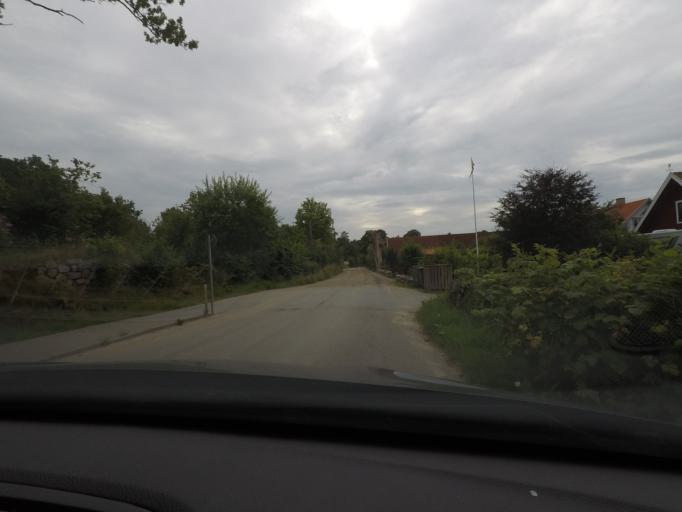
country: SE
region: Skane
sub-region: Osby Kommun
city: Osby
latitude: 56.3628
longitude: 14.0006
